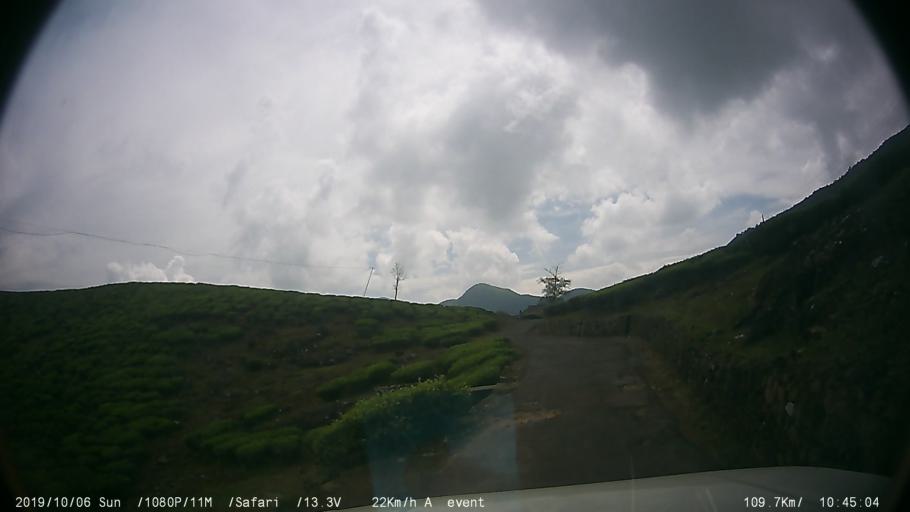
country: IN
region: Kerala
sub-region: Kottayam
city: Erattupetta
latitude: 9.6203
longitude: 76.9527
